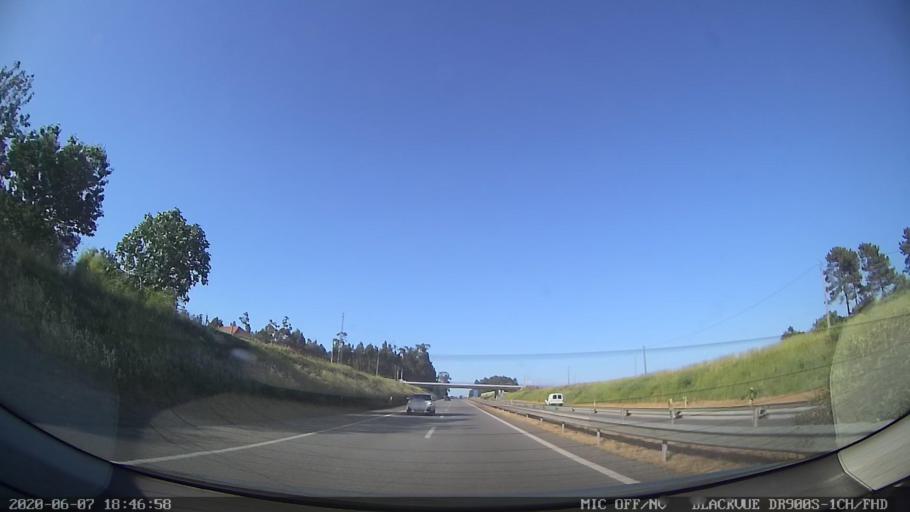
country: PT
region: Braga
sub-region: Vila Nova de Famalicao
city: Vila Nova de Famalicao
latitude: 41.3953
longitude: -8.4725
